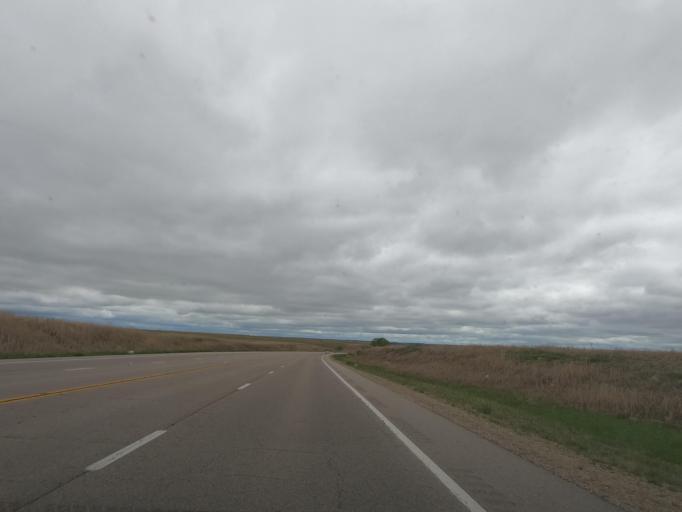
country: US
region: Kansas
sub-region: Greenwood County
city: Eureka
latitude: 37.6436
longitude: -96.4259
